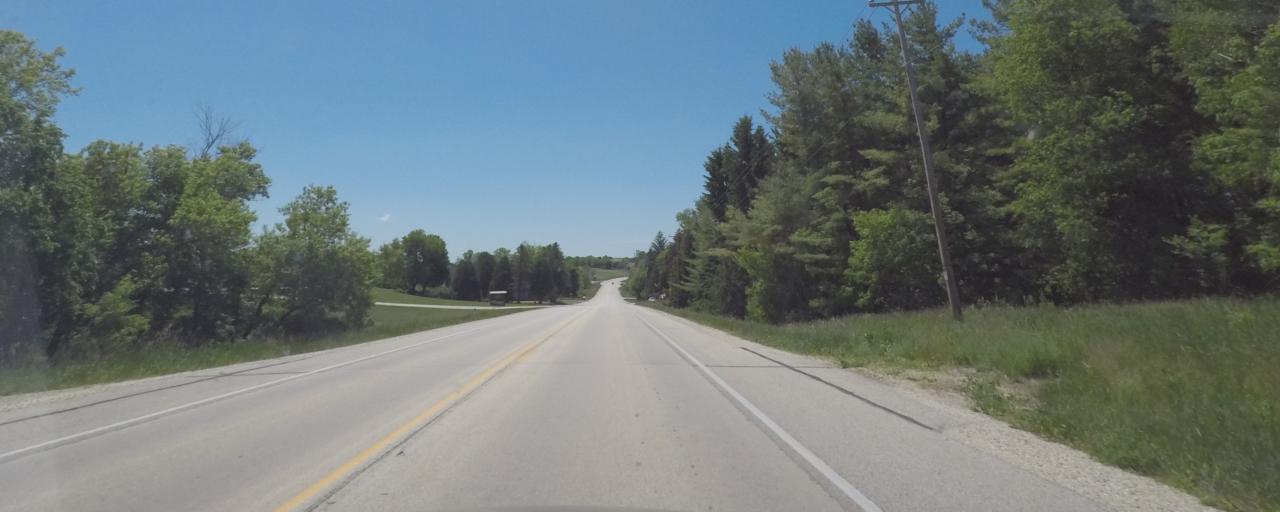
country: US
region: Wisconsin
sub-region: Ozaukee County
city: Kohler
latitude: 43.5327
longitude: -88.0945
